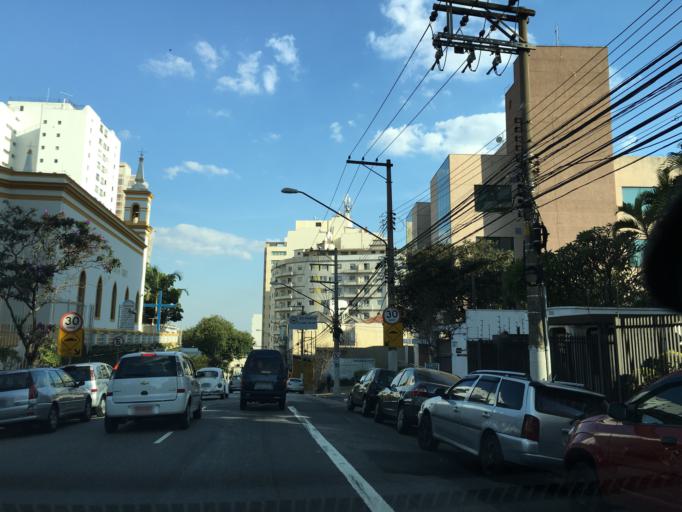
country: BR
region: Sao Paulo
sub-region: Sao Paulo
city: Sao Paulo
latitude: -23.4963
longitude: -46.6259
